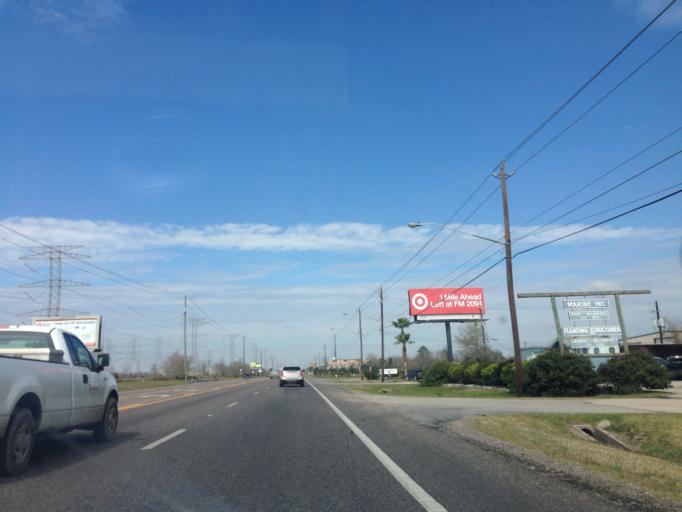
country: US
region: Texas
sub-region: Galveston County
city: Kemah
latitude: 29.5276
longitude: -95.0119
